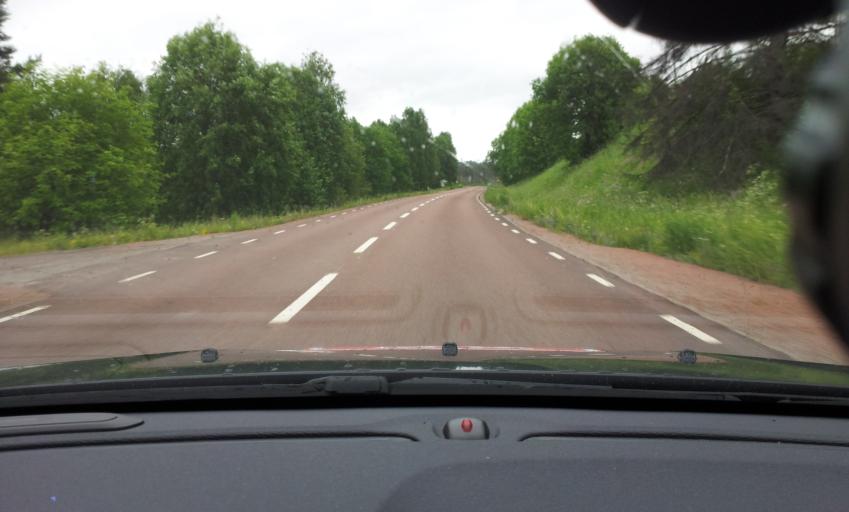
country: SE
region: Jaemtland
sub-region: Ragunda Kommun
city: Hammarstrand
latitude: 63.0585
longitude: 16.4079
